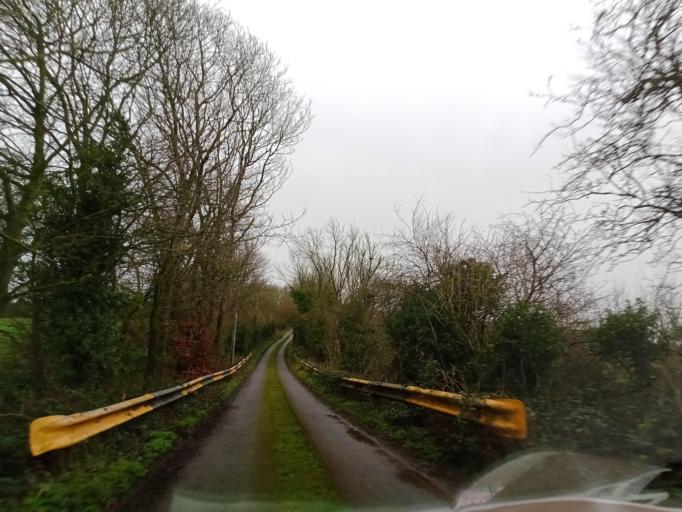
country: IE
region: Munster
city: Fethard
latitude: 52.5595
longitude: -7.7091
